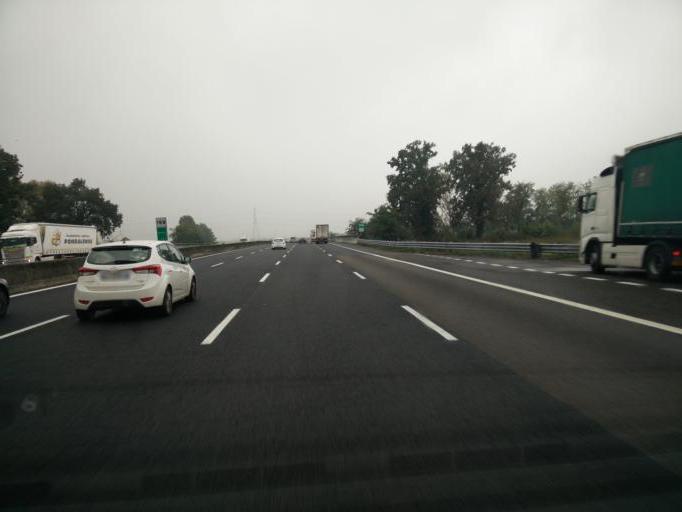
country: IT
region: Emilia-Romagna
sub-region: Provincia di Modena
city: San Damaso
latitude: 44.5852
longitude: 10.9630
